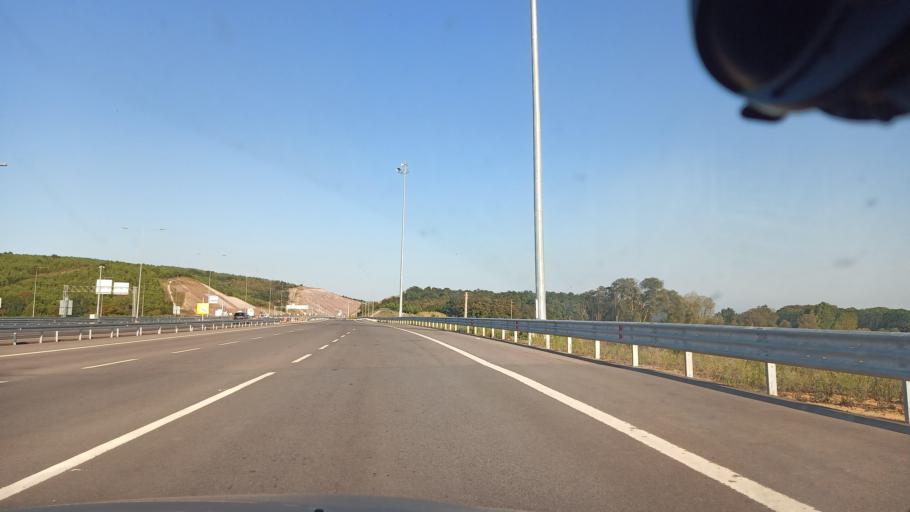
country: TR
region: Sakarya
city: Adapazari
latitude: 40.8390
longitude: 30.3640
